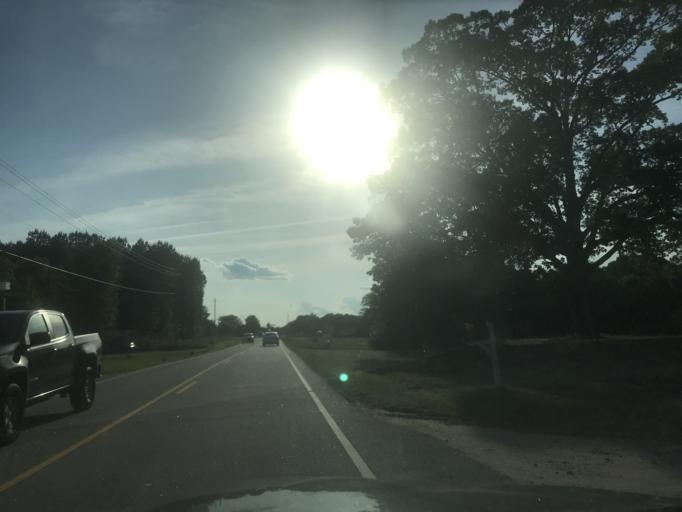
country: US
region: North Carolina
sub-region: Wake County
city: Knightdale
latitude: 35.7513
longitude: -78.4760
